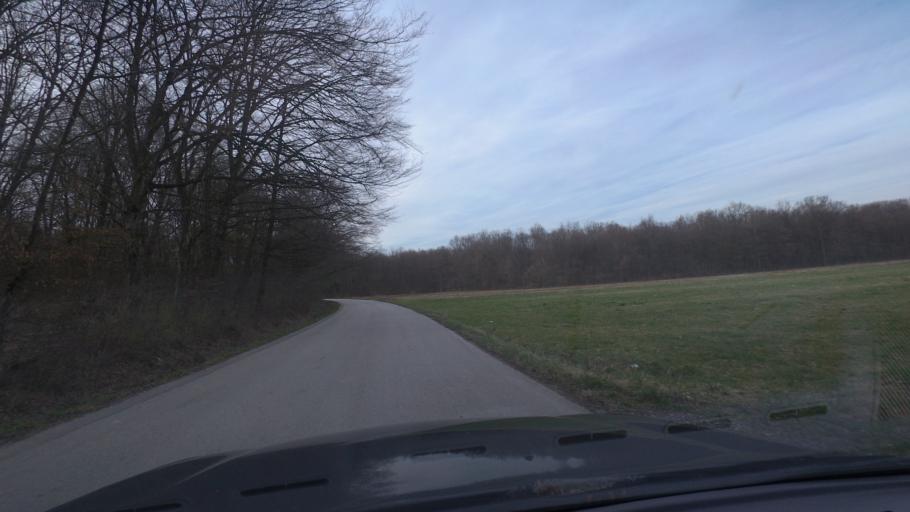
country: HR
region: Grad Zagreb
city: Horvati
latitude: 45.6999
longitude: 15.8362
